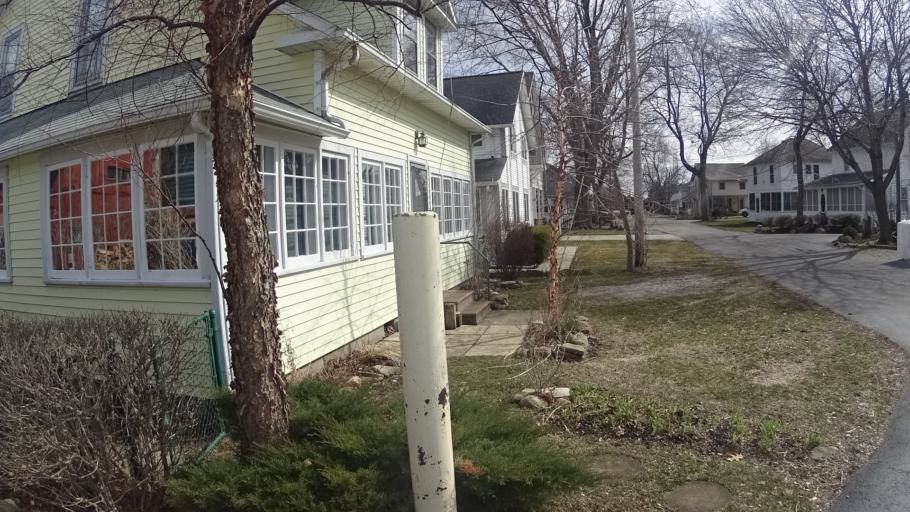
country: US
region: Ohio
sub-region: Erie County
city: Huron
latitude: 41.3849
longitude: -82.4640
